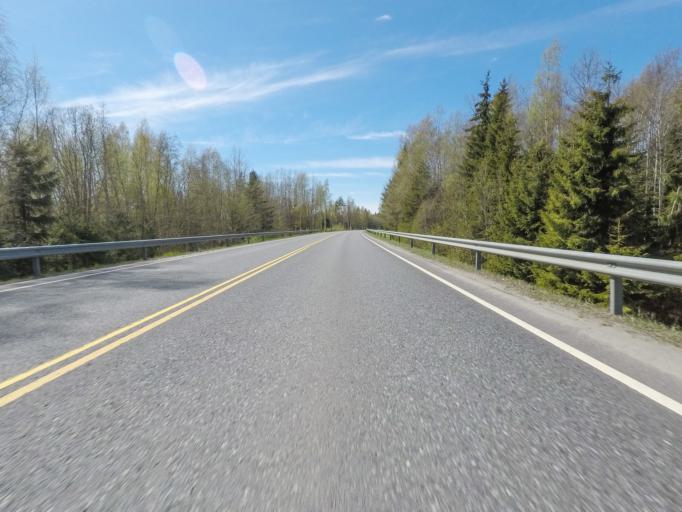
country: FI
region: Haeme
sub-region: Forssa
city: Humppila
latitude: 60.9807
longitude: 23.4379
